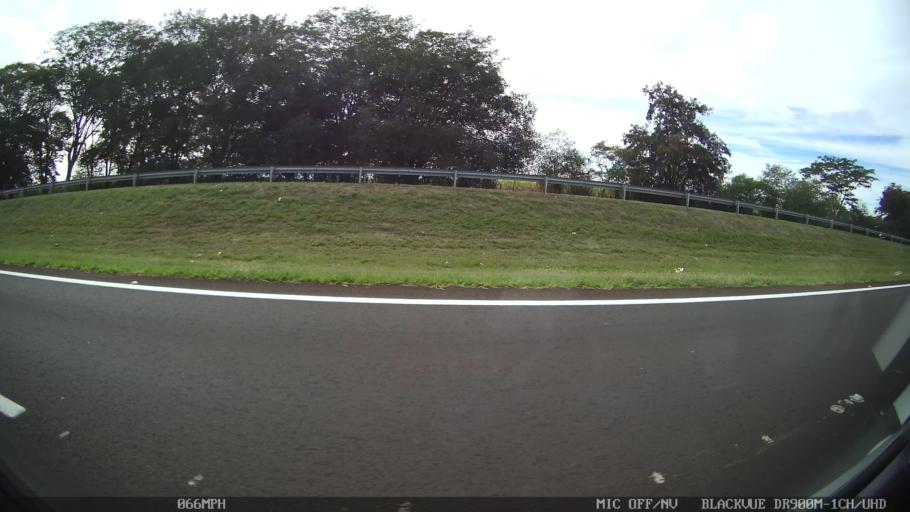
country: BR
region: Sao Paulo
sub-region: Taquaritinga
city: Taquaritinga
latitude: -21.4702
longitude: -48.6065
